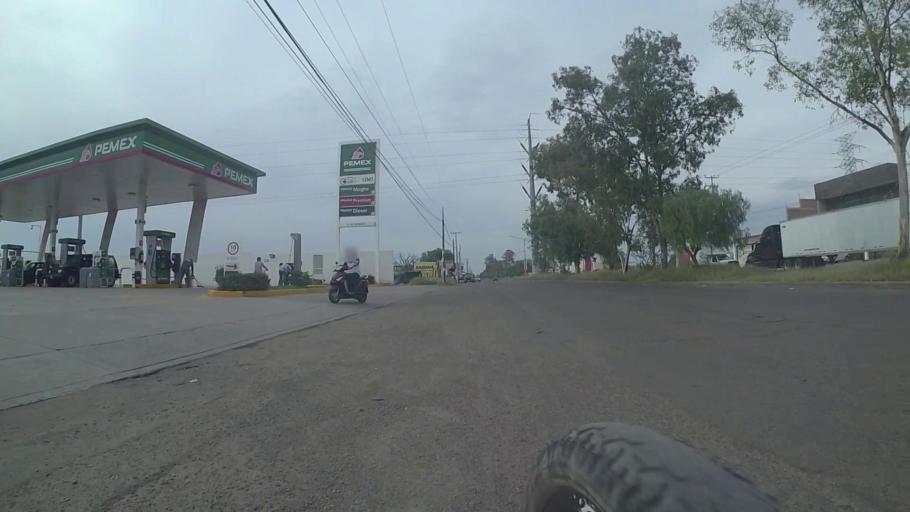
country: MX
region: Aguascalientes
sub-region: Aguascalientes
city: San Sebastian [Fraccionamiento]
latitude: 21.8345
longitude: -102.2936
